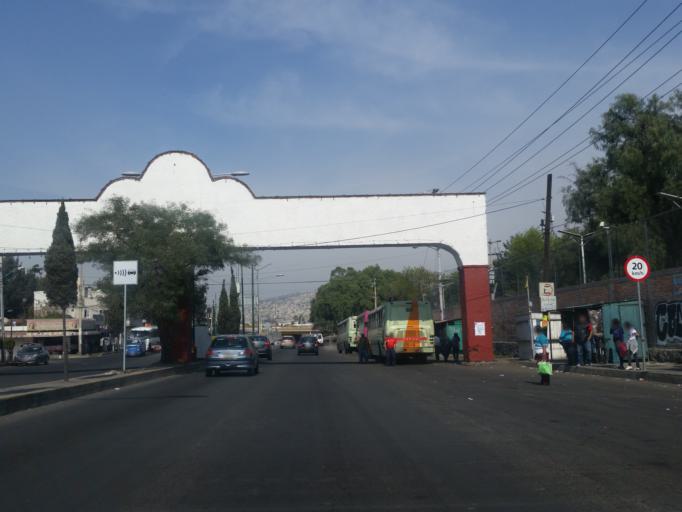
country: MX
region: Mexico
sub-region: La Paz
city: San Isidro
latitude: 19.3211
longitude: -98.9594
